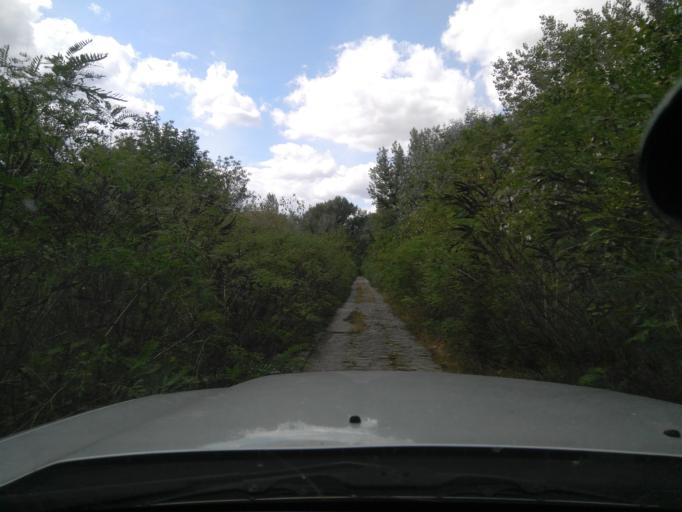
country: HU
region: Bacs-Kiskun
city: Apostag
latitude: 46.8949
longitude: 18.9439
